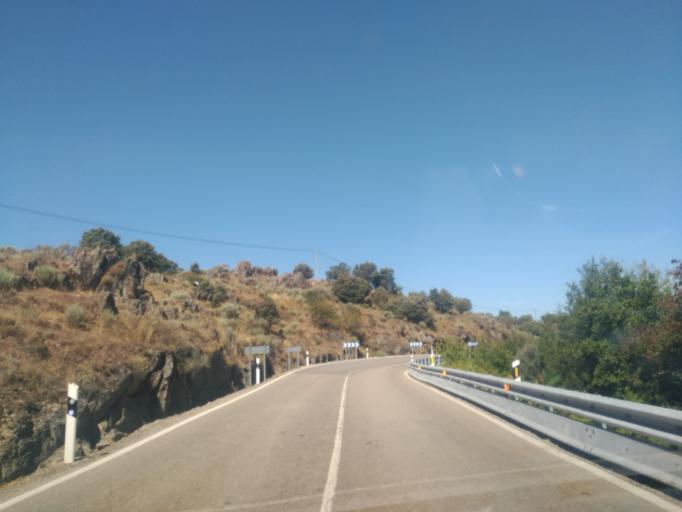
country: ES
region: Castille and Leon
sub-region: Provincia de Zamora
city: Villardeciervos
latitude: 41.9805
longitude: -6.2314
